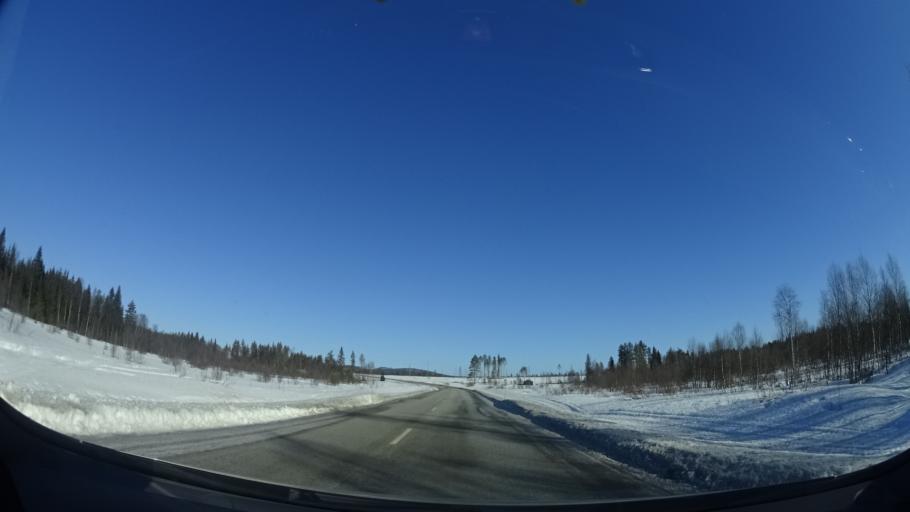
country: SE
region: Vaesterbotten
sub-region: Skelleftea Kommun
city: Langsele
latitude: 65.0946
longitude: 20.0886
